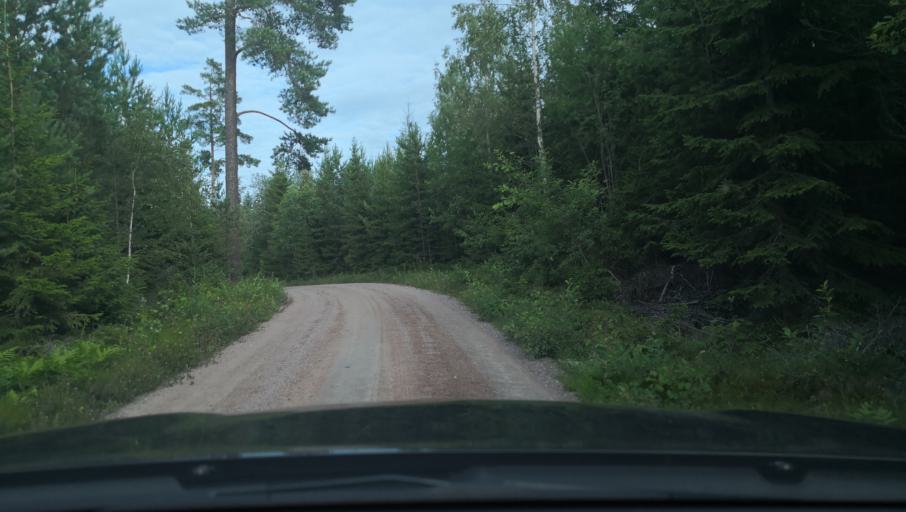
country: SE
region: Vaestmanland
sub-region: Surahammars Kommun
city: Surahammar
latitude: 59.6580
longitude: 16.1484
